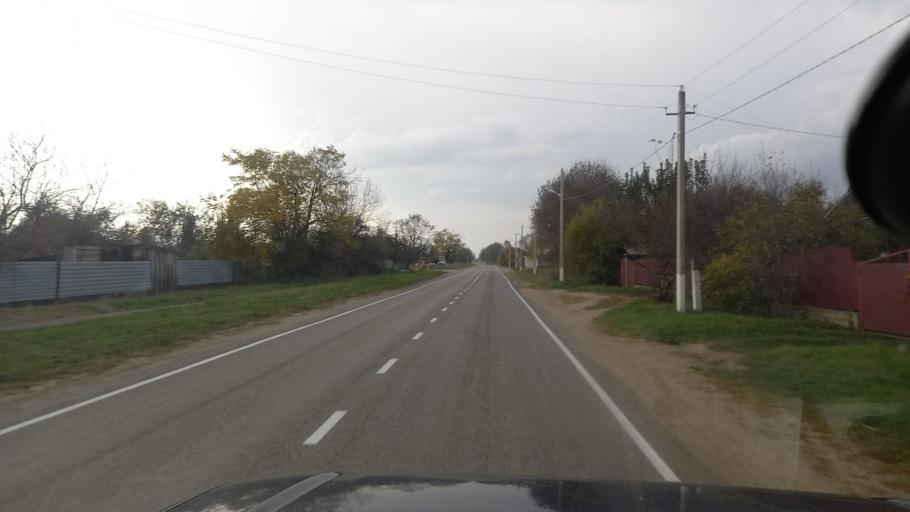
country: RU
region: Krasnodarskiy
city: Gubskaya
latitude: 44.3179
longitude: 40.6219
